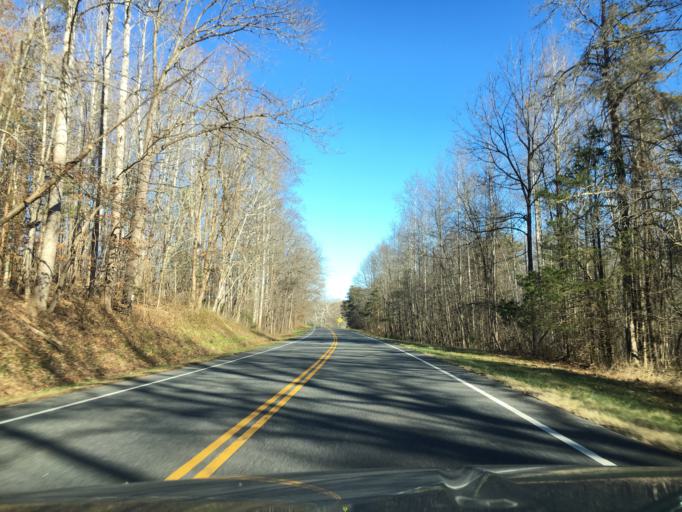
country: US
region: Virginia
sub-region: Appomattox County
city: Appomattox
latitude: 37.3782
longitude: -78.7899
